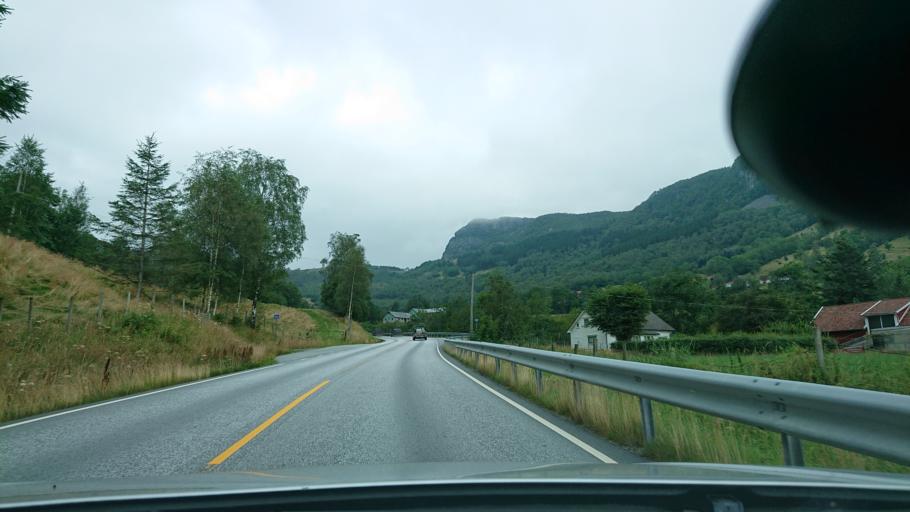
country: NO
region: Rogaland
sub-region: Hjelmeland
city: Hjelmelandsvagen
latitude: 59.1643
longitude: 6.1710
